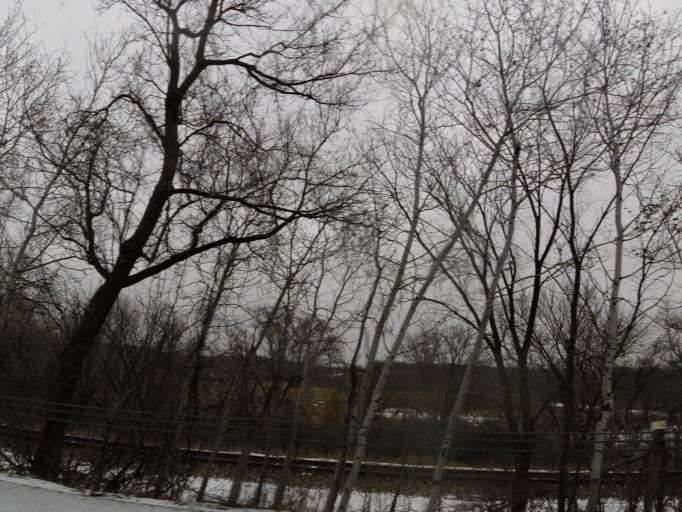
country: US
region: Minnesota
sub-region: Hennepin County
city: Independence
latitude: 45.0257
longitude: -93.7116
